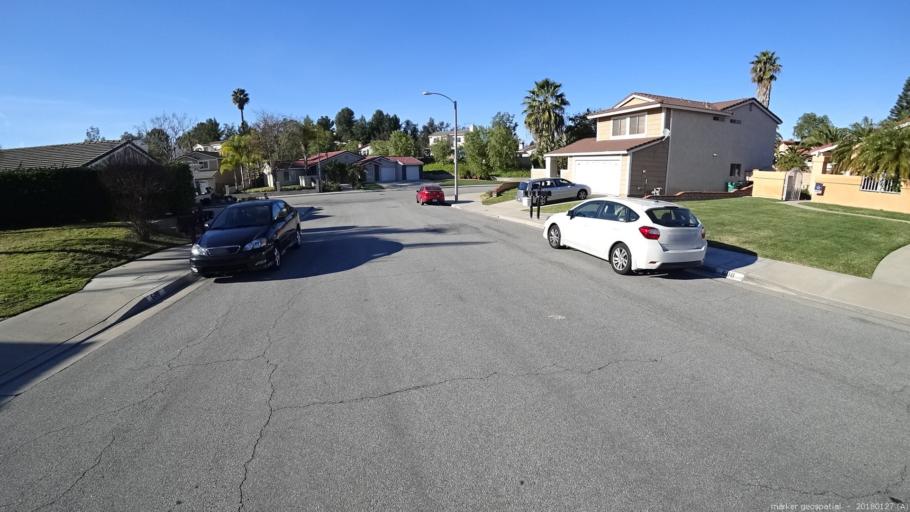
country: US
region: California
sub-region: Los Angeles County
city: Diamond Bar
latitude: 34.0166
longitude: -117.7915
